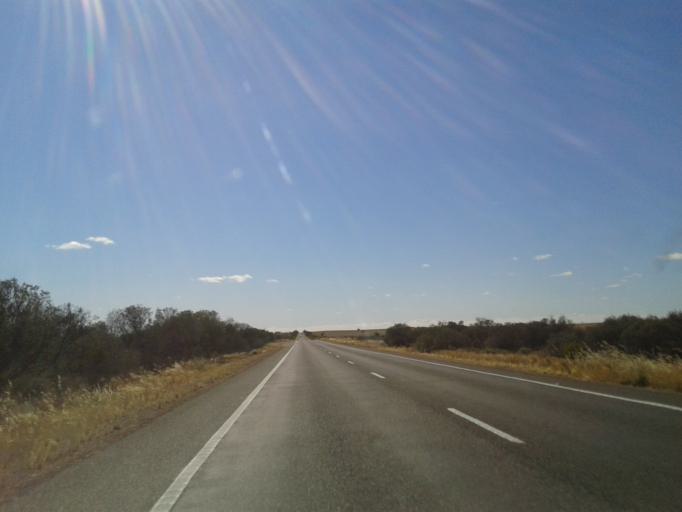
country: AU
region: South Australia
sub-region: Renmark Paringa
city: Renmark
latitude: -34.2750
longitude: 141.1611
